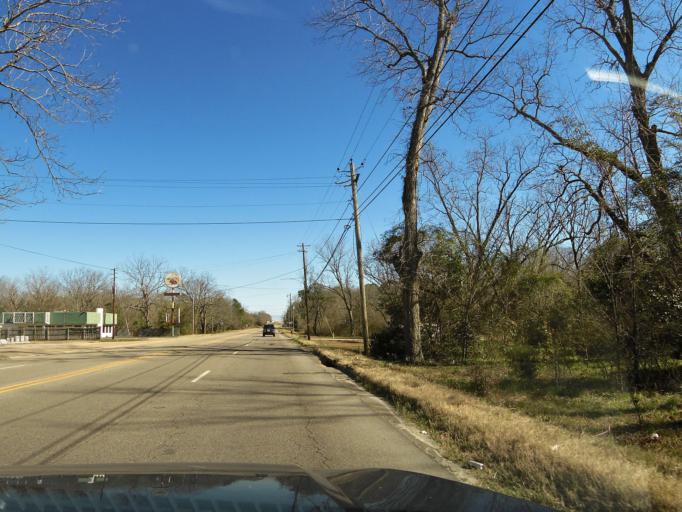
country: US
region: Alabama
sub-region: Bullock County
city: Union Springs
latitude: 32.1462
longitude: -85.7071
